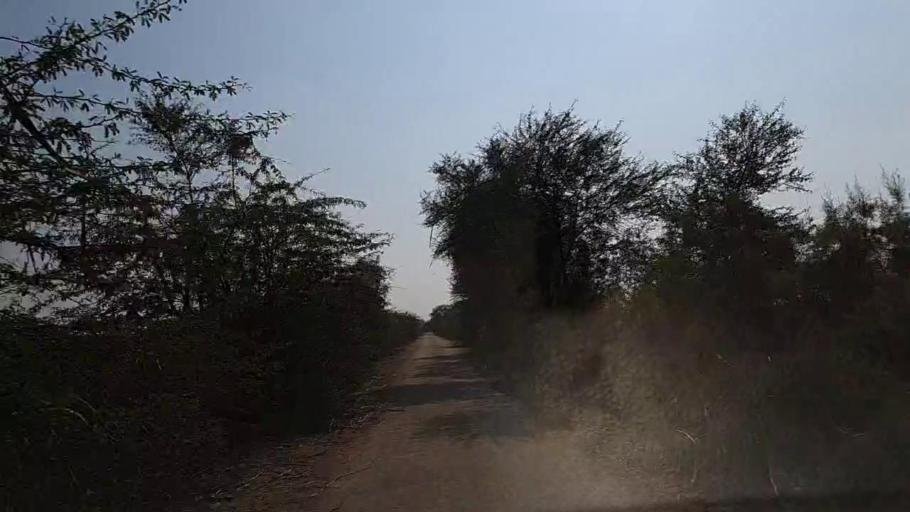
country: PK
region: Sindh
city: Jam Sahib
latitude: 26.2645
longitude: 68.5287
